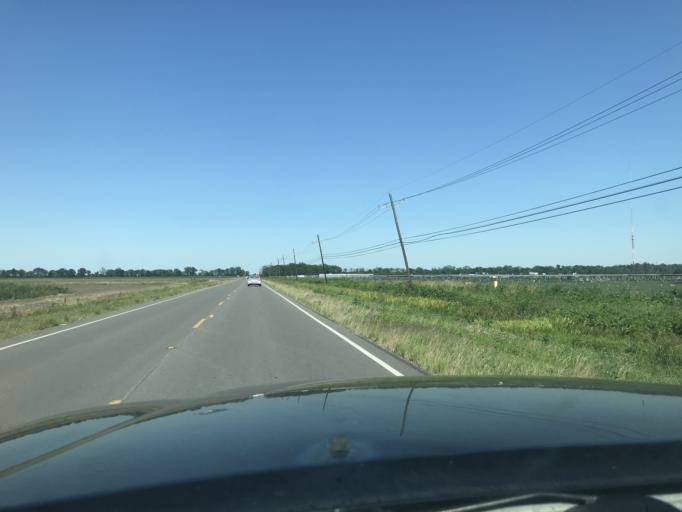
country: US
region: Louisiana
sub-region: West Baton Rouge Parish
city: Erwinville
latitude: 30.4686
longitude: -91.3347
